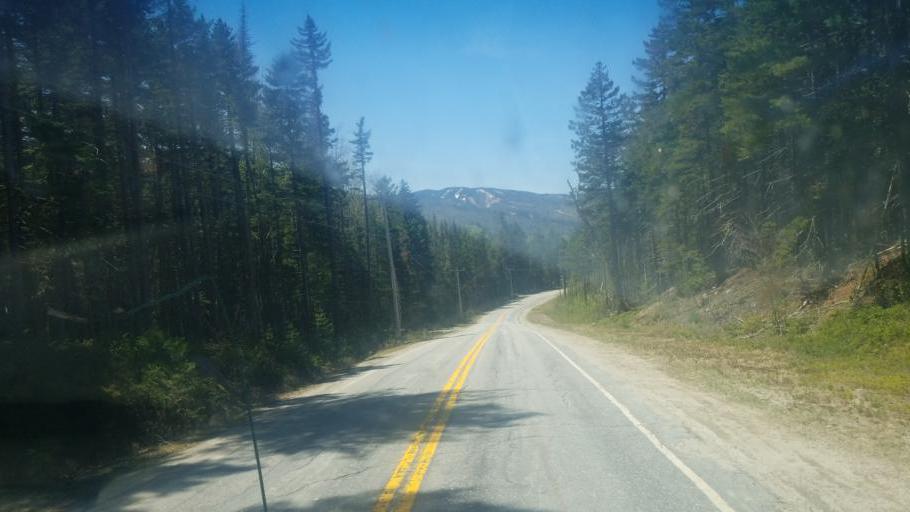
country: US
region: New Hampshire
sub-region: Coos County
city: Jefferson
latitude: 44.2657
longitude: -71.4187
